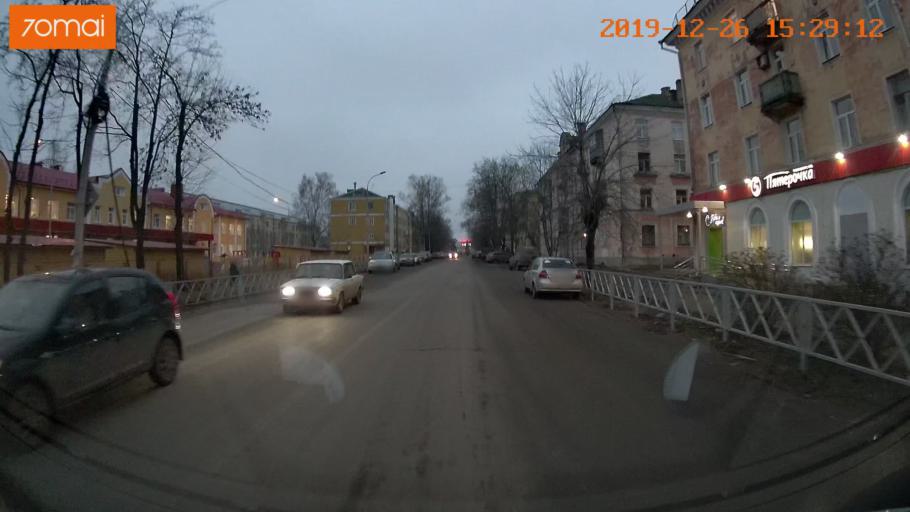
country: RU
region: Jaroslavl
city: Rybinsk
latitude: 58.0583
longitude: 38.8170
